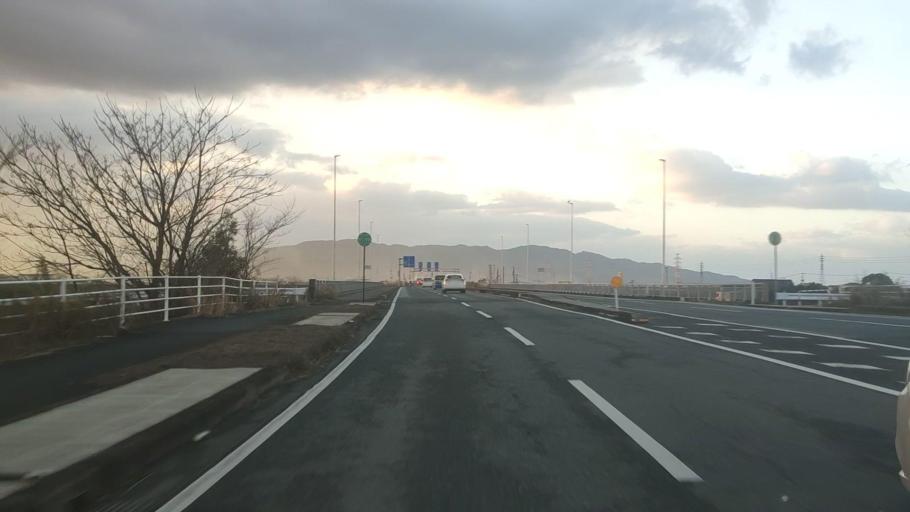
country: JP
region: Kumamoto
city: Kumamoto
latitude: 32.7412
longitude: 130.7047
